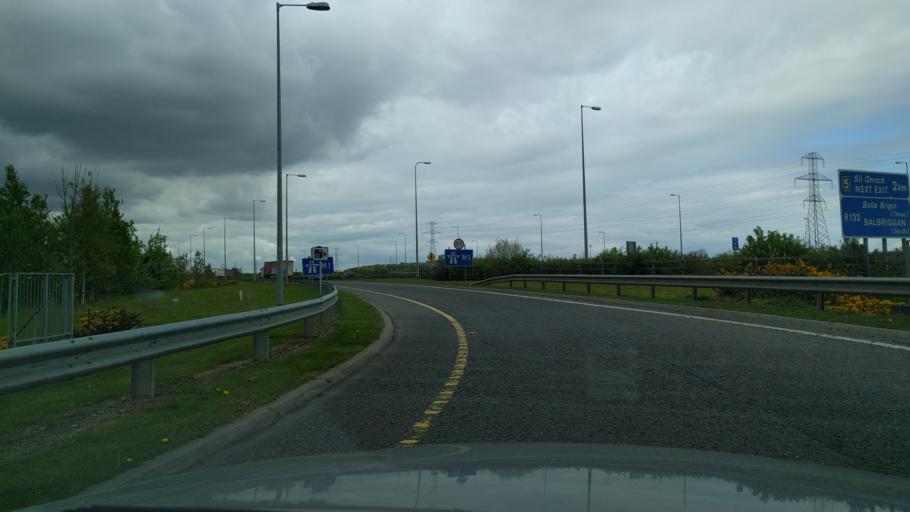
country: IE
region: Leinster
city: Lusk
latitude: 53.5382
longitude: -6.2126
